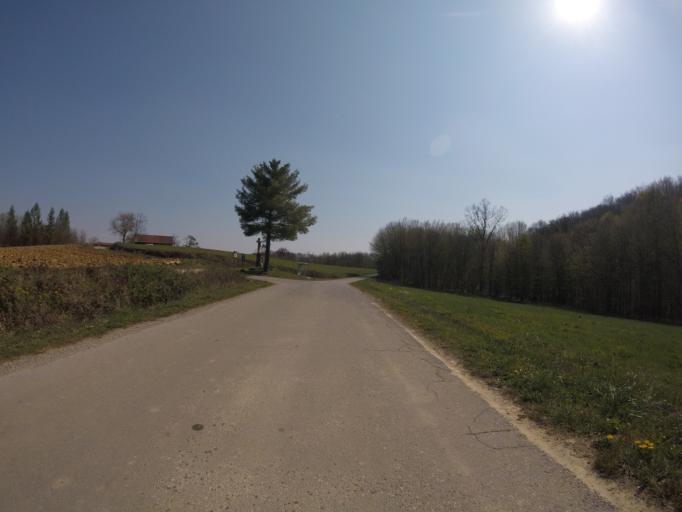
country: HR
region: Grad Zagreb
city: Strmec
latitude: 45.5796
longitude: 15.9196
